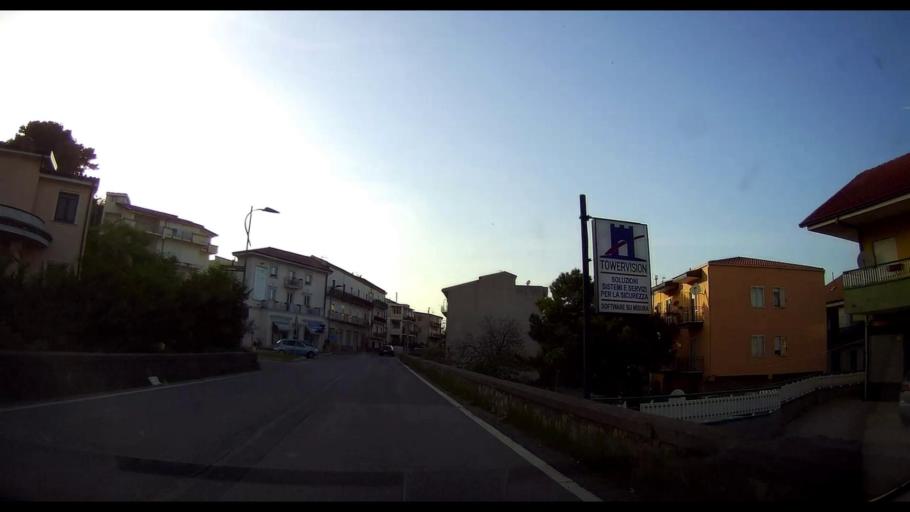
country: IT
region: Calabria
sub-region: Provincia di Crotone
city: Torretta
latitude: 39.4471
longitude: 17.0421
